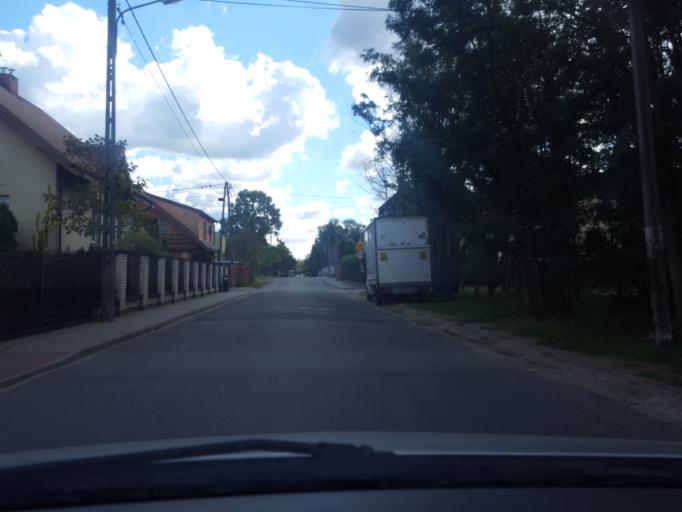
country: PL
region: Masovian Voivodeship
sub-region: Warszawa
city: Rembertow
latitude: 52.2739
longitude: 21.1627
